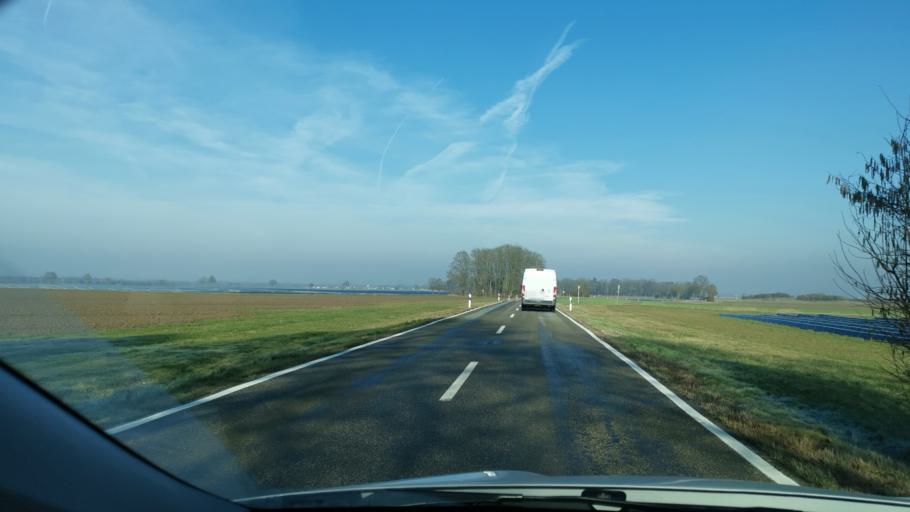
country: DE
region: Bavaria
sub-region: Swabia
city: Munster
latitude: 48.6319
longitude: 10.9267
